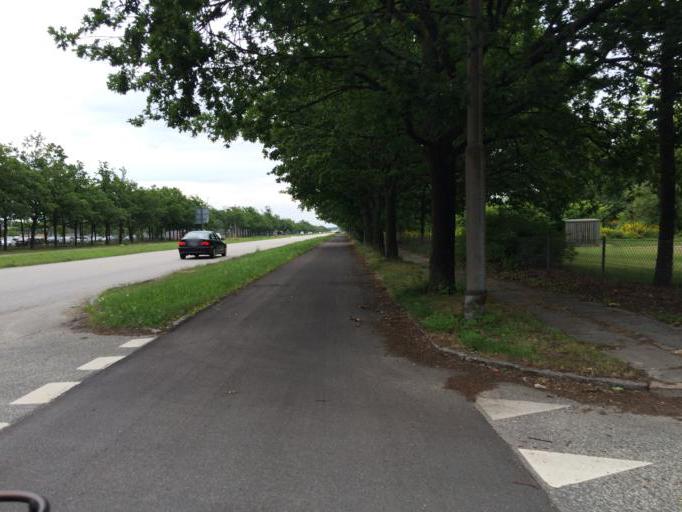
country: DK
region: Capital Region
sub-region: Hvidovre Kommune
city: Hvidovre
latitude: 55.6139
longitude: 12.4772
